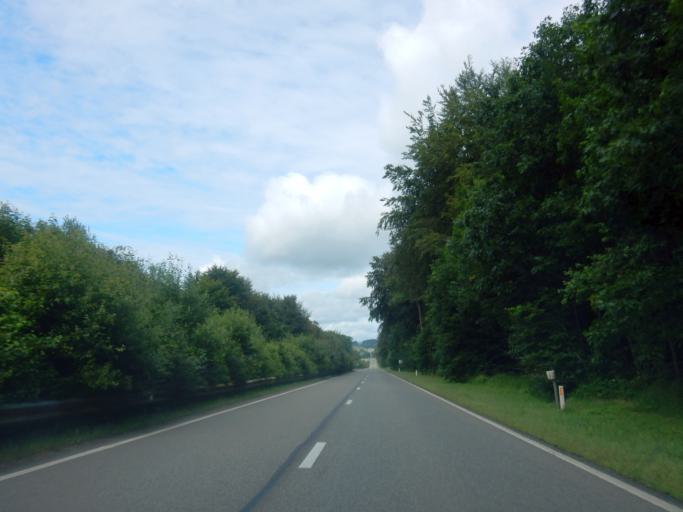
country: BE
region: Wallonia
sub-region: Province du Luxembourg
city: Paliseul
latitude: 49.8623
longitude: 5.1863
